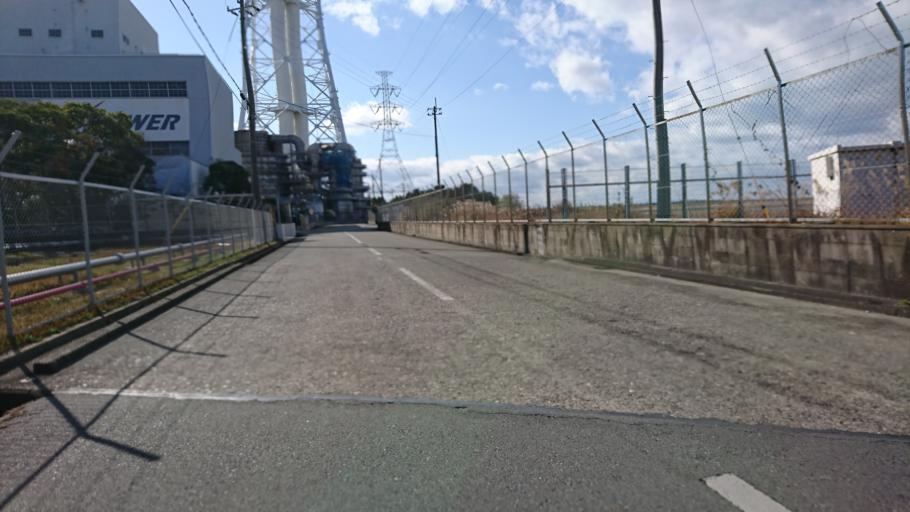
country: JP
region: Hyogo
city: Shirahamacho-usazakiminami
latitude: 34.7555
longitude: 134.7662
